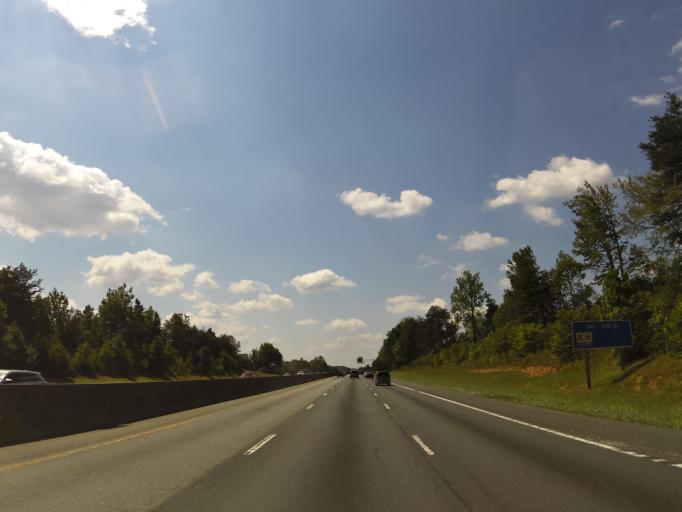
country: US
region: North Carolina
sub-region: Gaston County
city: Lowell
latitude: 35.2633
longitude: -81.1235
